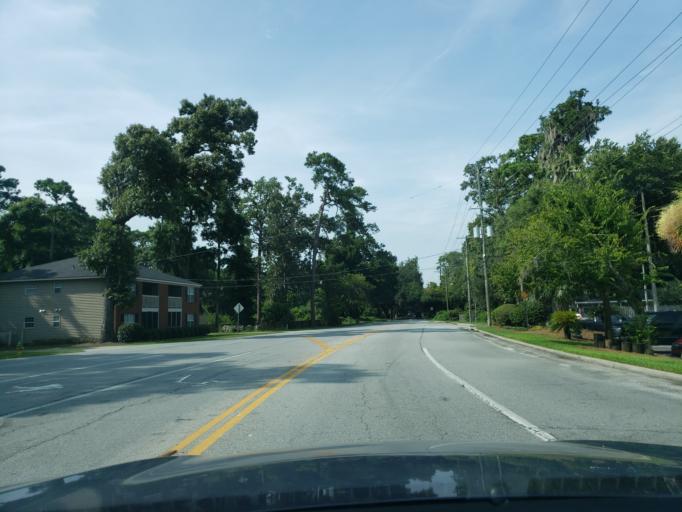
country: US
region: Georgia
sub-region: Chatham County
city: Wilmington Island
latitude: 32.0315
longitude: -80.9642
